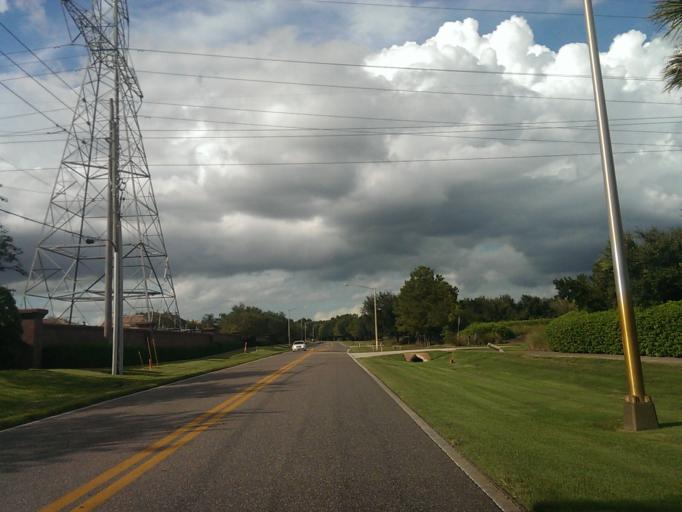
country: US
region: Florida
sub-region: Orange County
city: Bay Hill
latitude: 28.4687
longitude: -81.5412
